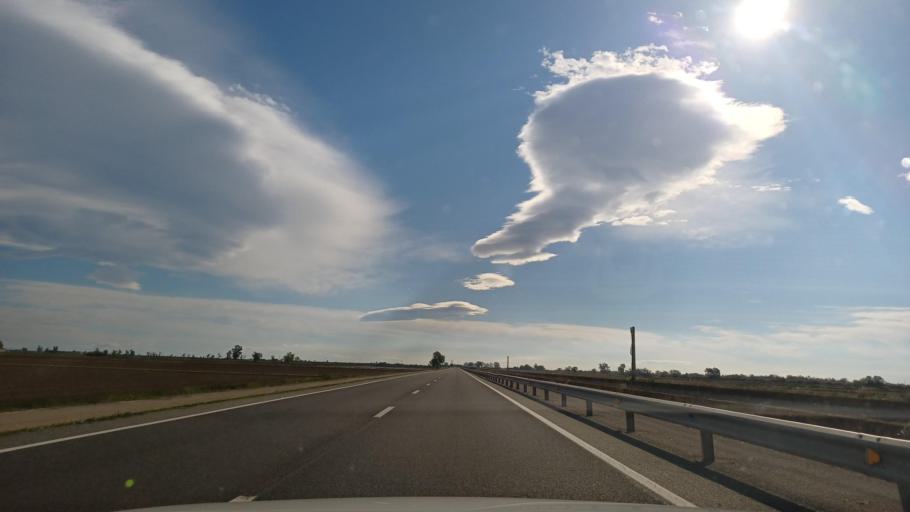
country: ES
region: Catalonia
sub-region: Provincia de Tarragona
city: Amposta
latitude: 40.7140
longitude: 0.6238
